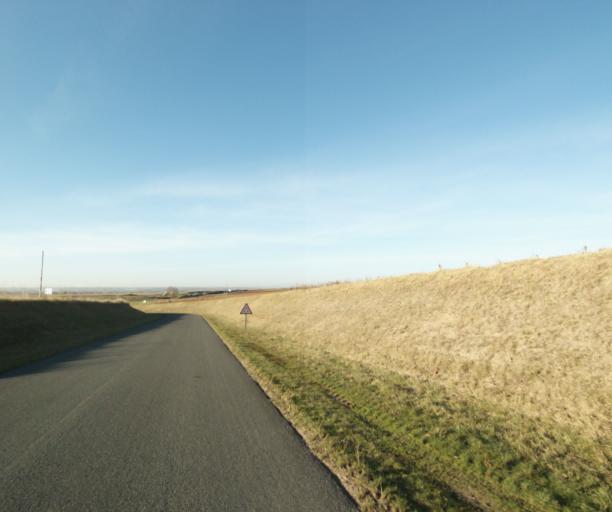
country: FR
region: Poitou-Charentes
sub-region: Departement de la Charente-Maritime
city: Cherac
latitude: 45.7007
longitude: -0.4444
